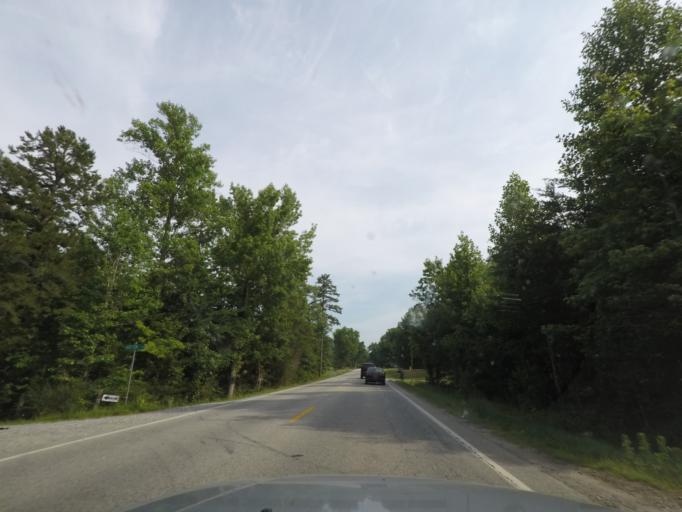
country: US
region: Virginia
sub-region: Prince Edward County
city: Hampden Sydney
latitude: 37.1606
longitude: -78.4393
